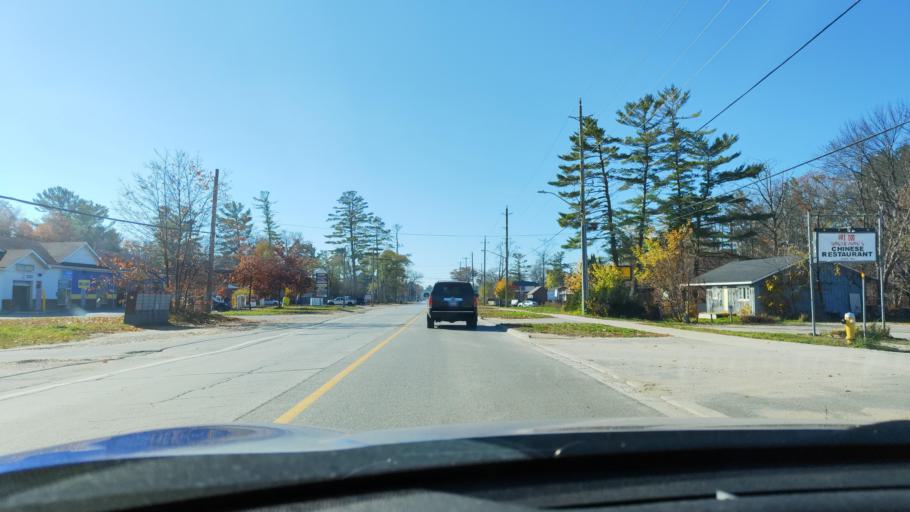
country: CA
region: Ontario
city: Wasaga Beach
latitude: 44.5261
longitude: -79.9973
